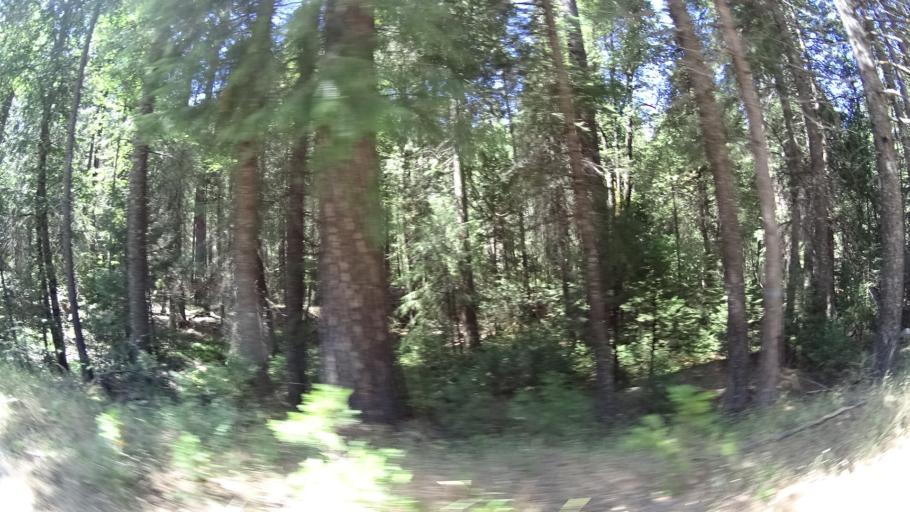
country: US
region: California
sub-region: Amador County
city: Pioneer
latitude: 38.4303
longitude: -120.4574
